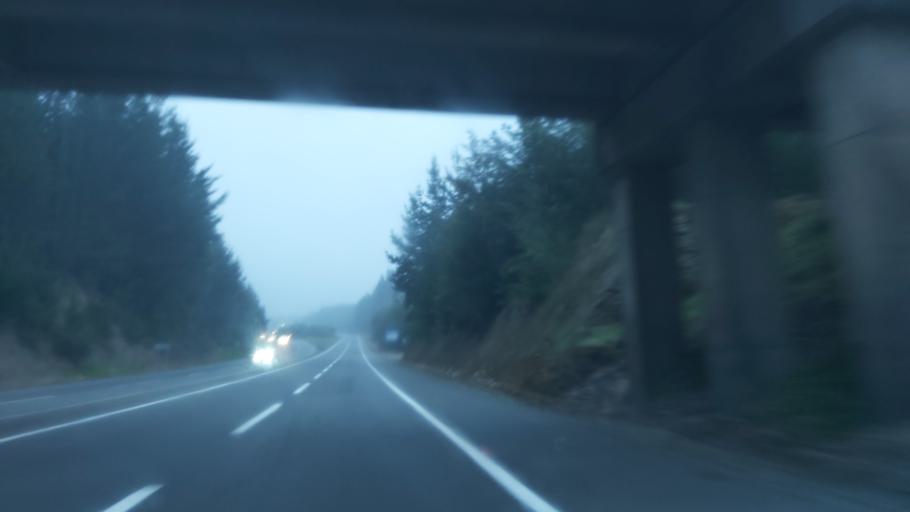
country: CL
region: Biobio
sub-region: Provincia de Concepcion
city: Penco
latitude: -36.7434
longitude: -72.9130
